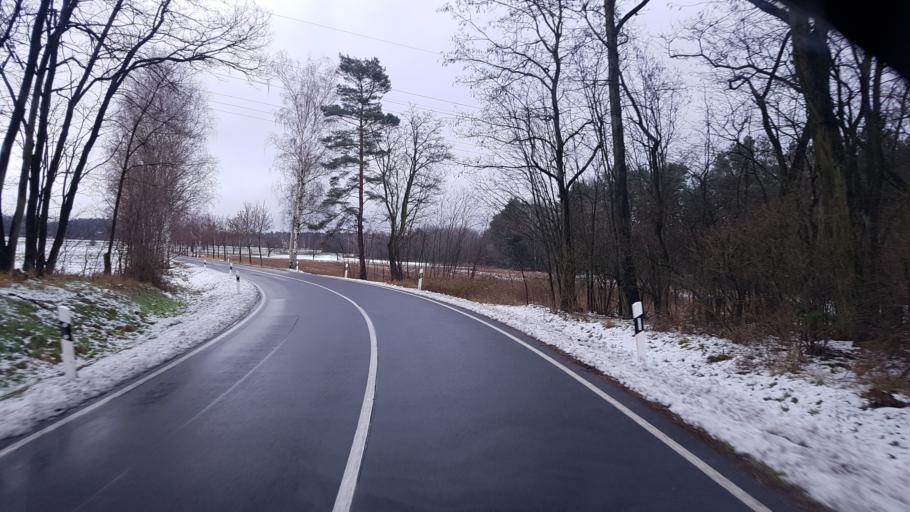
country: DE
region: Brandenburg
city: Schenkendobern
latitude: 51.9151
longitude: 14.6219
